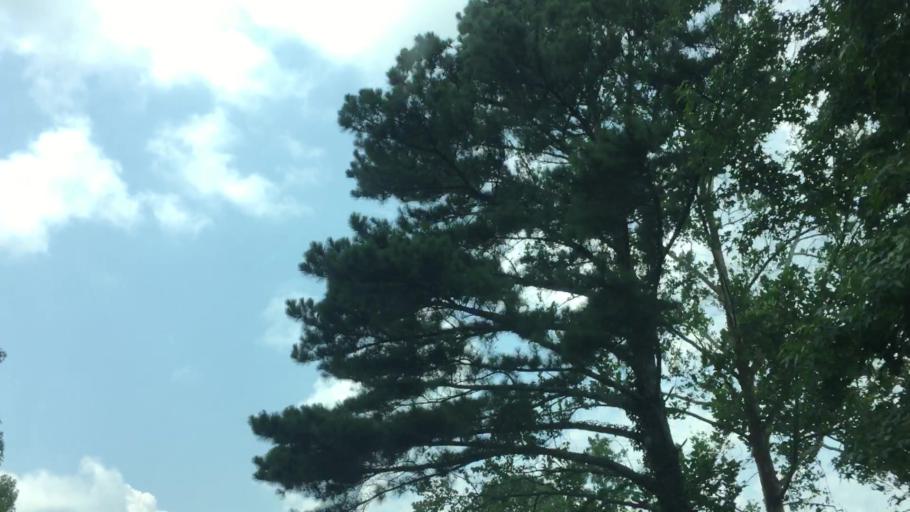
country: US
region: Georgia
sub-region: Fulton County
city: Chattahoochee Hills
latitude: 33.5791
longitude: -84.8112
